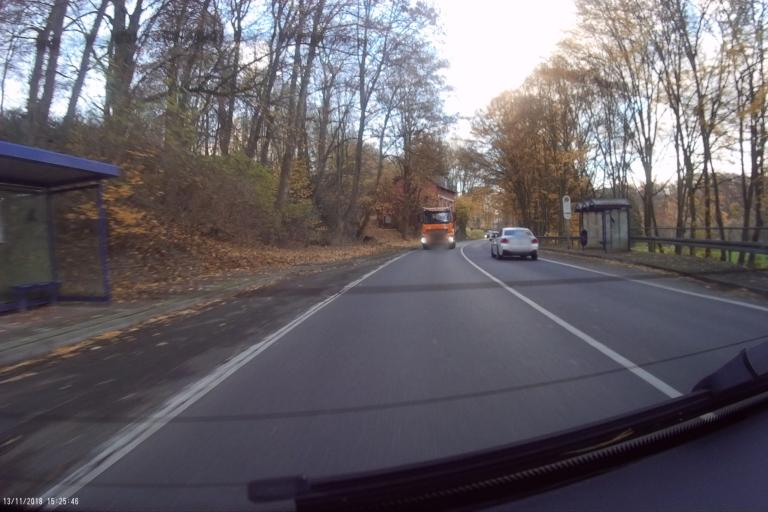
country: DE
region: North Rhine-Westphalia
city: Hattingen
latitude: 51.3820
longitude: 7.1944
